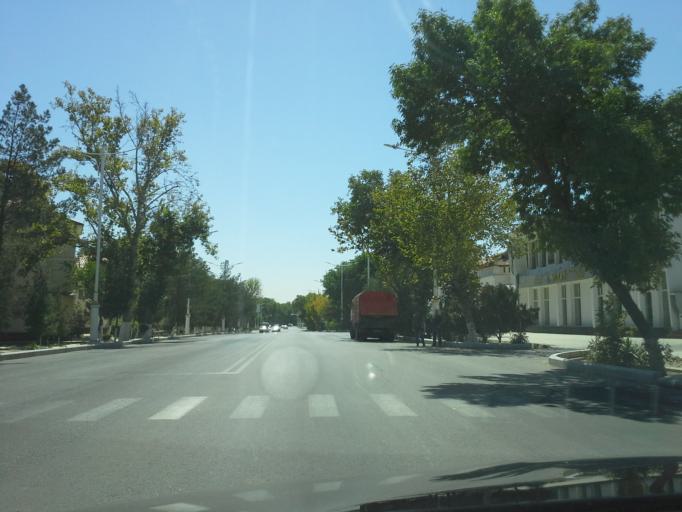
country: TM
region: Ahal
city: Ashgabat
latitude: 37.9478
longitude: 58.3502
